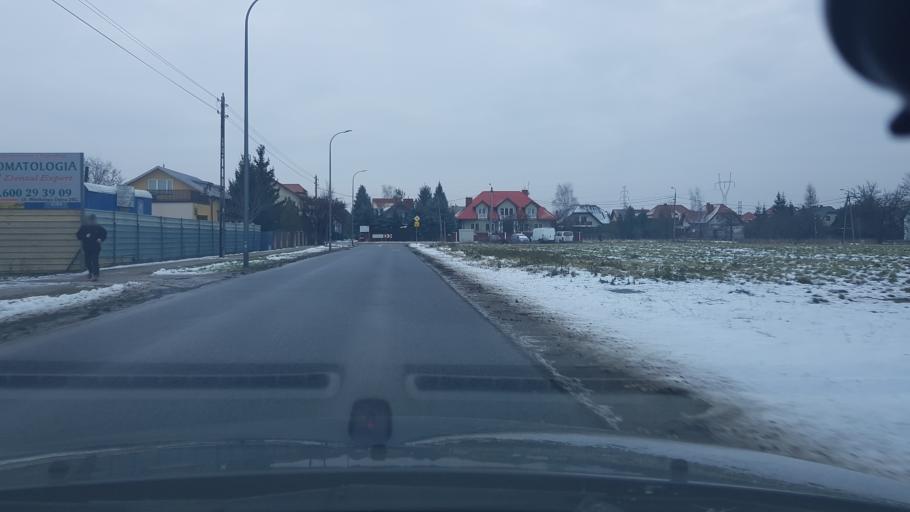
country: PL
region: Masovian Voivodeship
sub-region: Warszawa
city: Targowek
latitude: 52.3080
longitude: 21.0388
